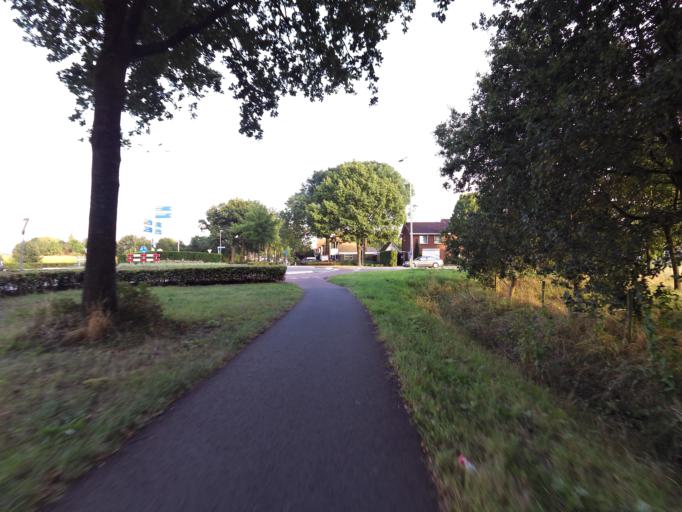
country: NL
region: Gelderland
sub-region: Gemeente Zevenaar
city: Zevenaar
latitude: 51.9097
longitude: 6.1060
